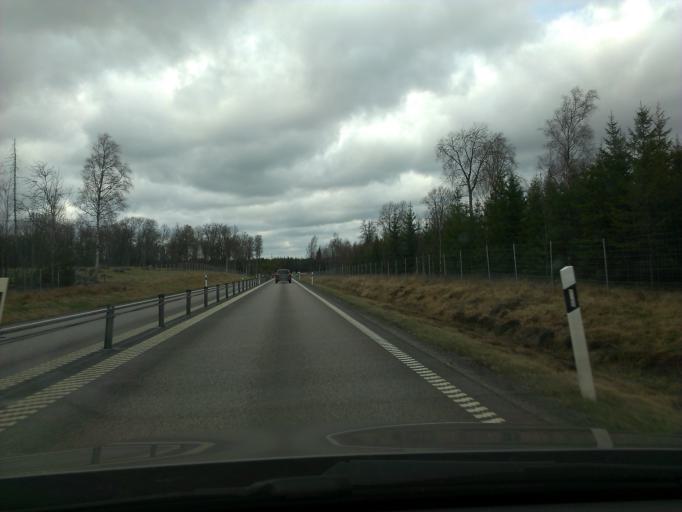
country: SE
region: Kronoberg
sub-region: Alvesta Kommun
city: Vislanda
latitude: 56.6784
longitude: 14.3156
